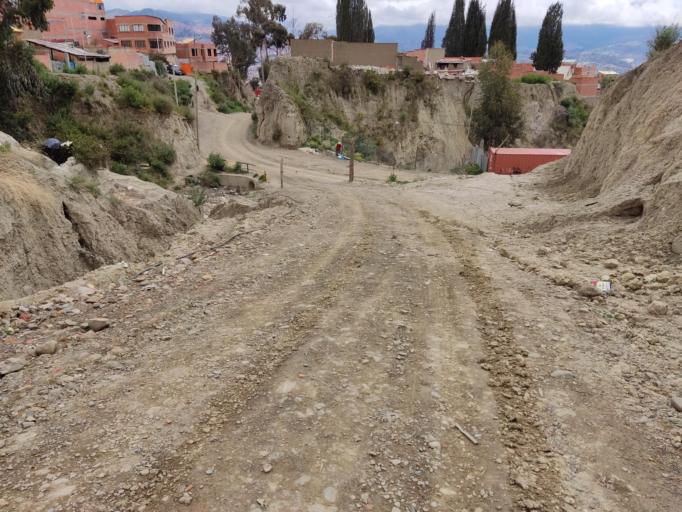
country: BO
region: La Paz
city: La Paz
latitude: -16.5352
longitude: -68.1357
